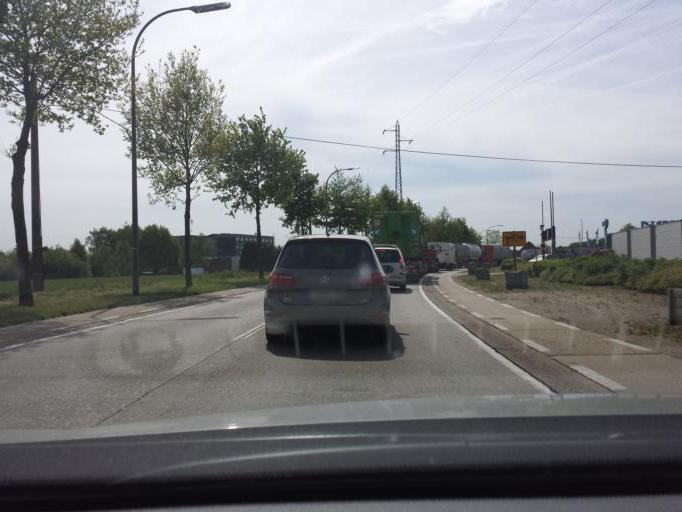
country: BE
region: Flanders
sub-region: Provincie Limburg
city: Beringen
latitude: 51.0446
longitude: 5.1902
